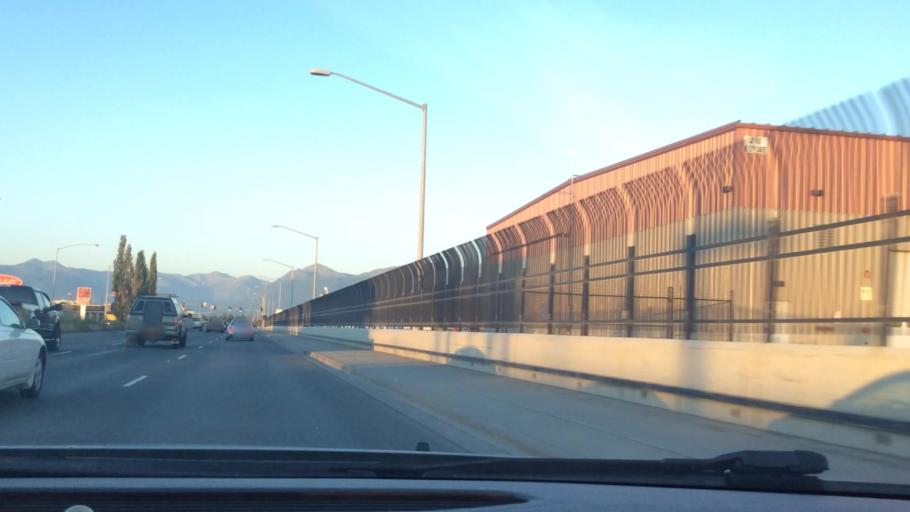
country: US
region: Alaska
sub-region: Anchorage Municipality
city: Anchorage
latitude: 61.2172
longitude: -149.8425
